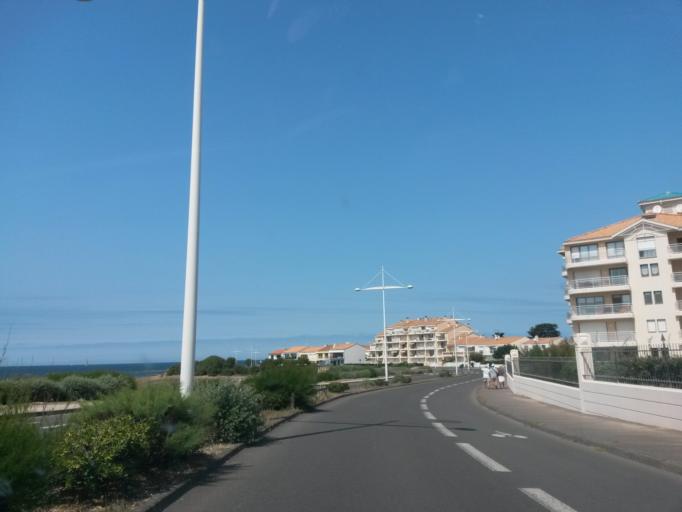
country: FR
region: Pays de la Loire
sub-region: Departement de la Vendee
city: Les Sables-d'Olonne
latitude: 46.4914
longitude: -1.8057
